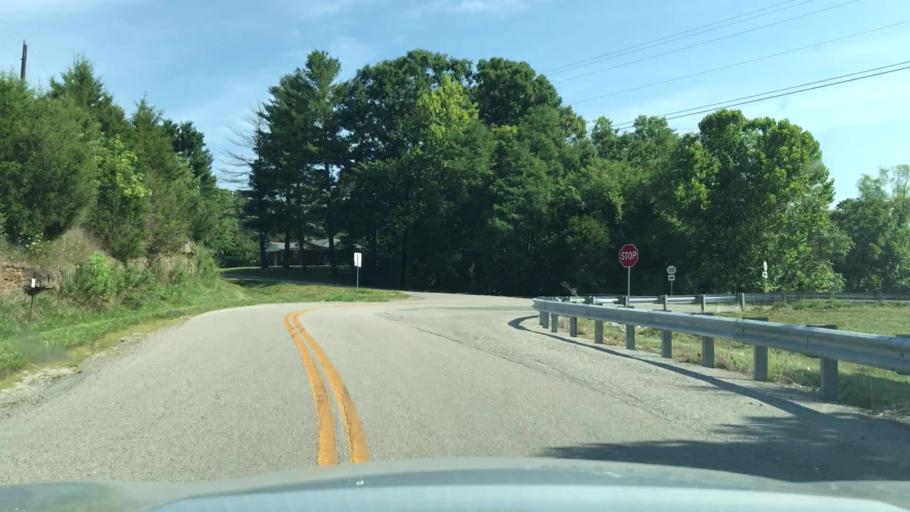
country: US
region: Kentucky
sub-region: Clinton County
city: Albany
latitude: 36.7487
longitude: -84.9914
